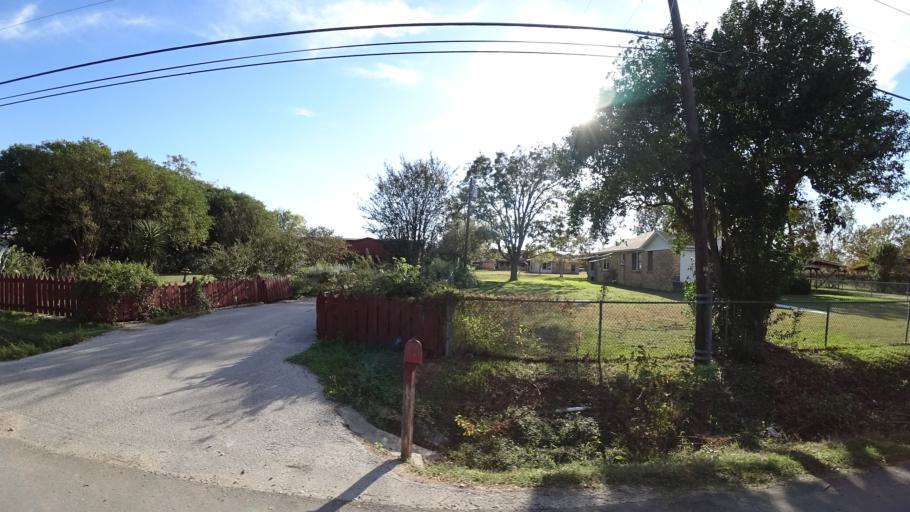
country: US
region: Texas
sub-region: Travis County
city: Wells Branch
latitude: 30.4726
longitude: -97.6802
